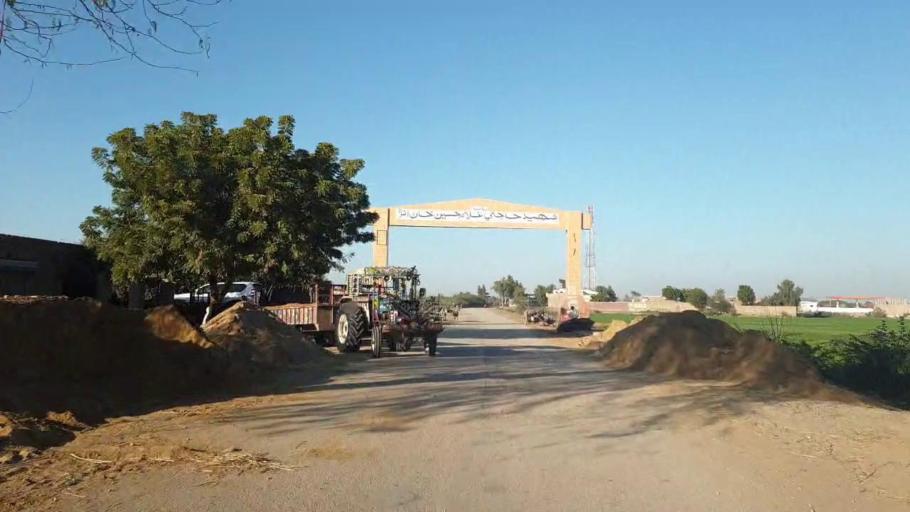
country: PK
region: Sindh
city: Dokri
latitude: 27.3656
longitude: 68.1156
